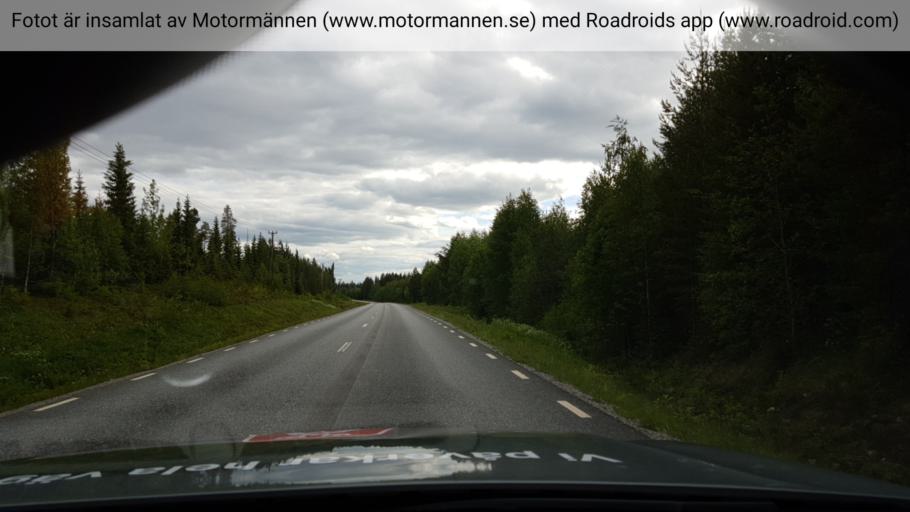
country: SE
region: Jaemtland
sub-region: Stroemsunds Kommun
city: Stroemsund
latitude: 63.9624
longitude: 15.4828
